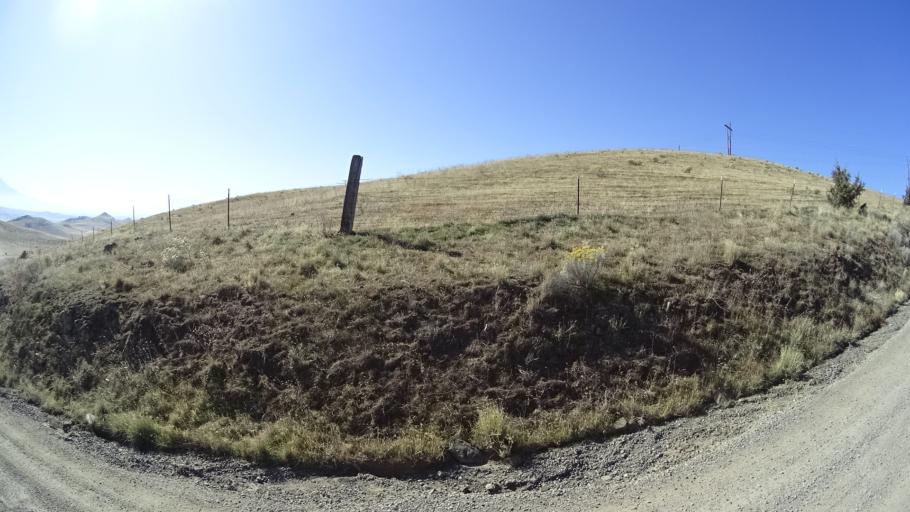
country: US
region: California
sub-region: Siskiyou County
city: Montague
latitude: 41.7673
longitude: -122.3574
